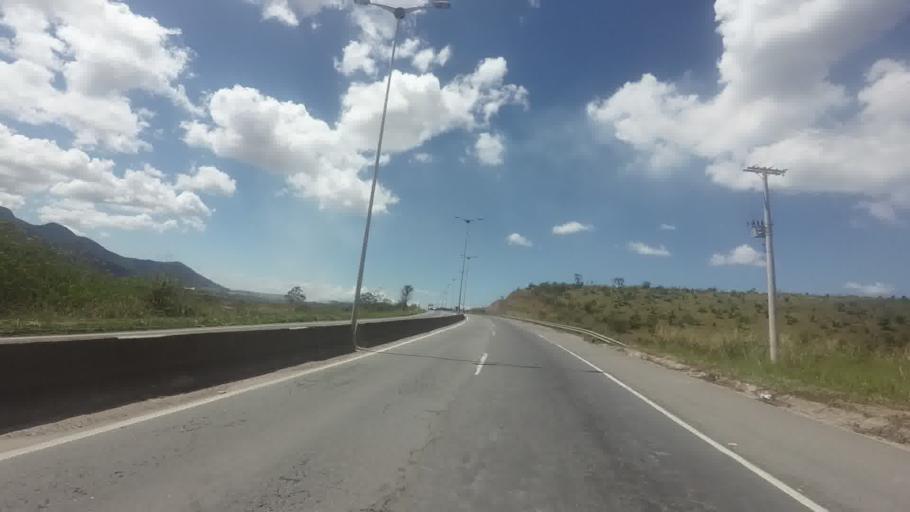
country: BR
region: Espirito Santo
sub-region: Serra
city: Serra
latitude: -20.2186
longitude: -40.3479
